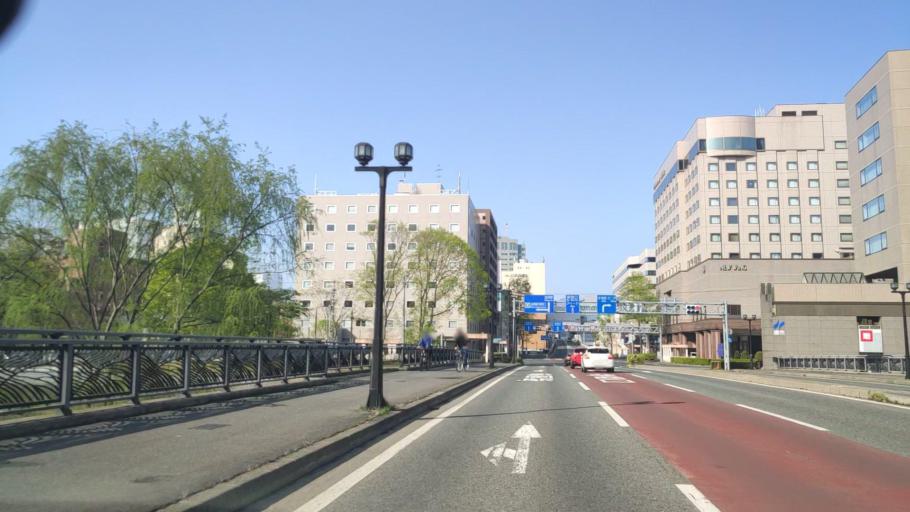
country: JP
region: Iwate
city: Morioka-shi
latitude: 39.7049
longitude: 141.1383
